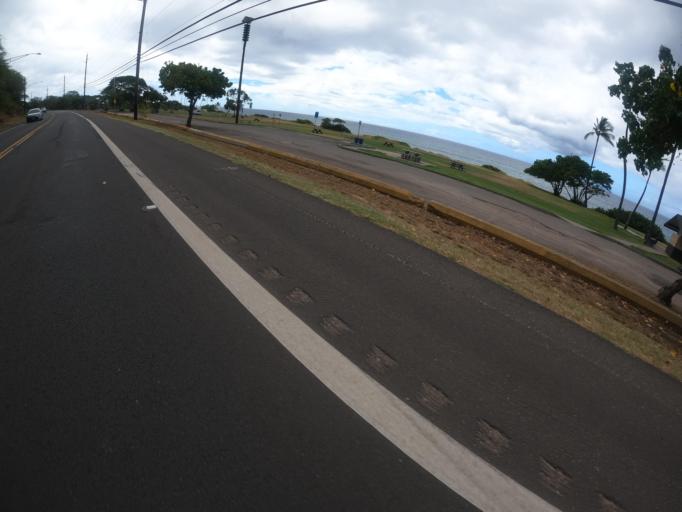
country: US
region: Hawaii
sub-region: Honolulu County
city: Makaha
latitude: 21.4868
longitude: -158.2295
